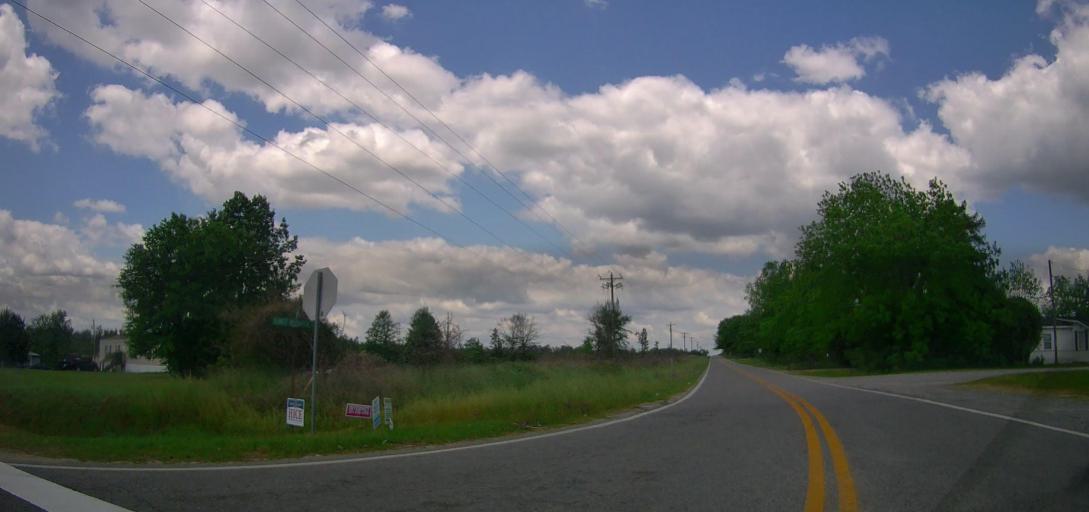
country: US
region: Georgia
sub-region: Laurens County
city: East Dublin
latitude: 32.5248
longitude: -82.8114
